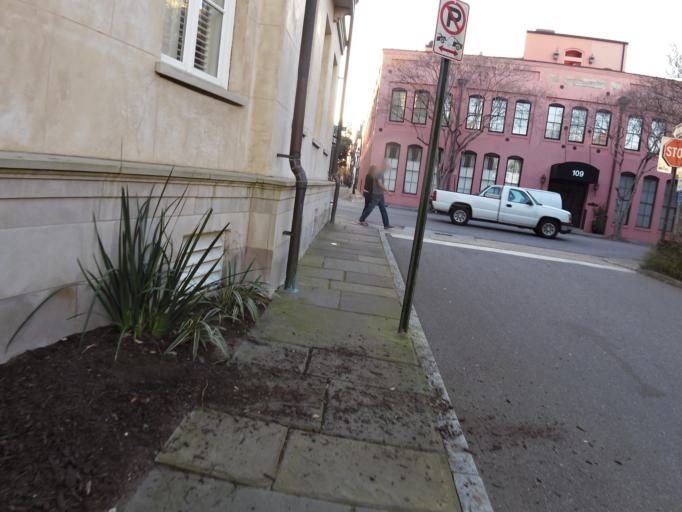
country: US
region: South Carolina
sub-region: Charleston County
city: Charleston
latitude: 32.7764
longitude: -79.9268
